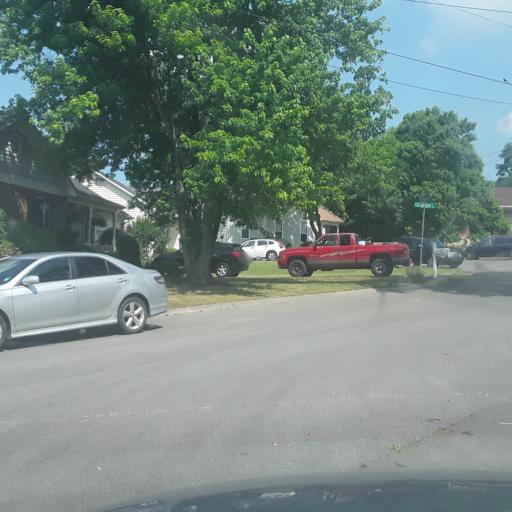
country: US
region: Tennessee
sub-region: Williamson County
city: Brentwood Estates
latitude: 36.0304
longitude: -86.7100
